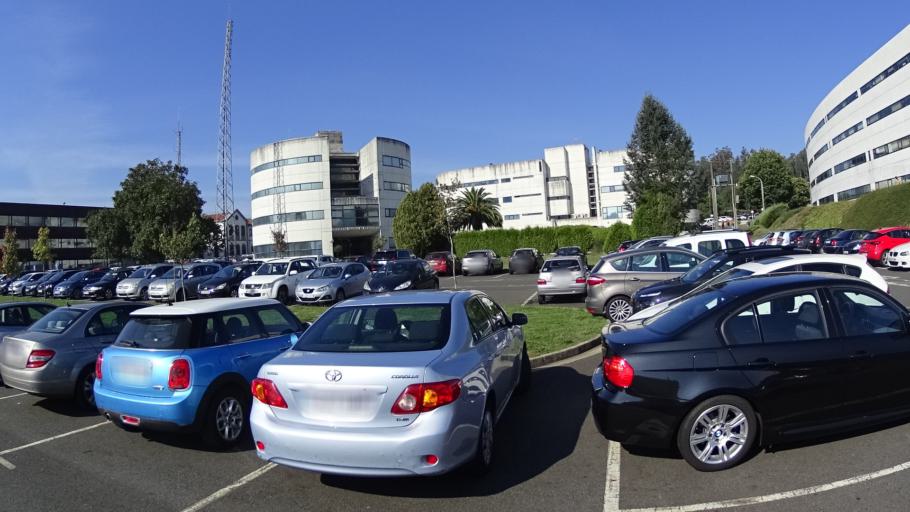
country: ES
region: Galicia
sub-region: Provincia da Coruna
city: Santiago de Compostela
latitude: 42.8877
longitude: -8.5175
